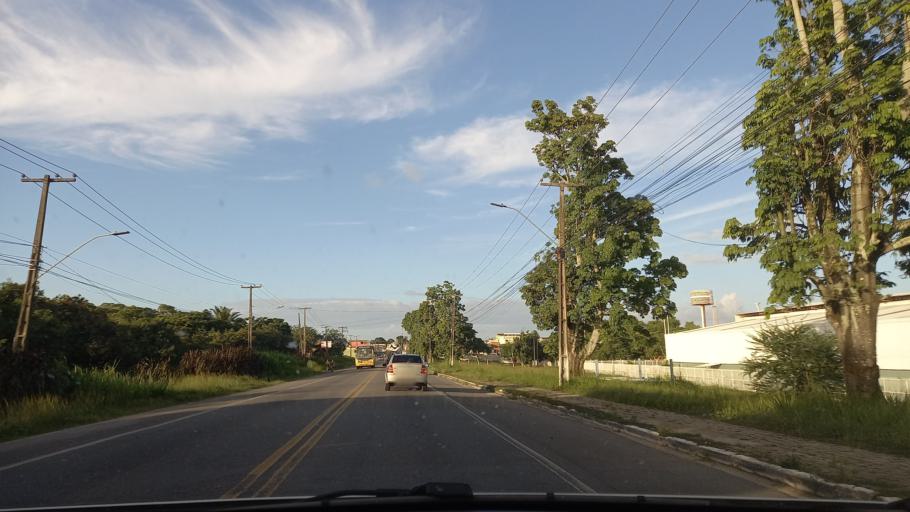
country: BR
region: Pernambuco
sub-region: Jaboatao Dos Guararapes
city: Jaboatao
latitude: -8.2283
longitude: -34.9713
